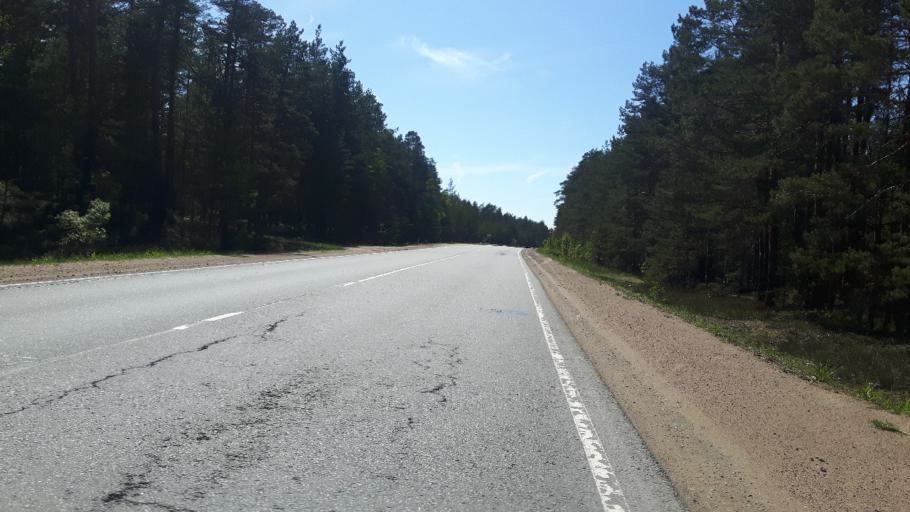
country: RU
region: Leningrad
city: Sista-Palkino
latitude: 59.7697
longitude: 28.8311
